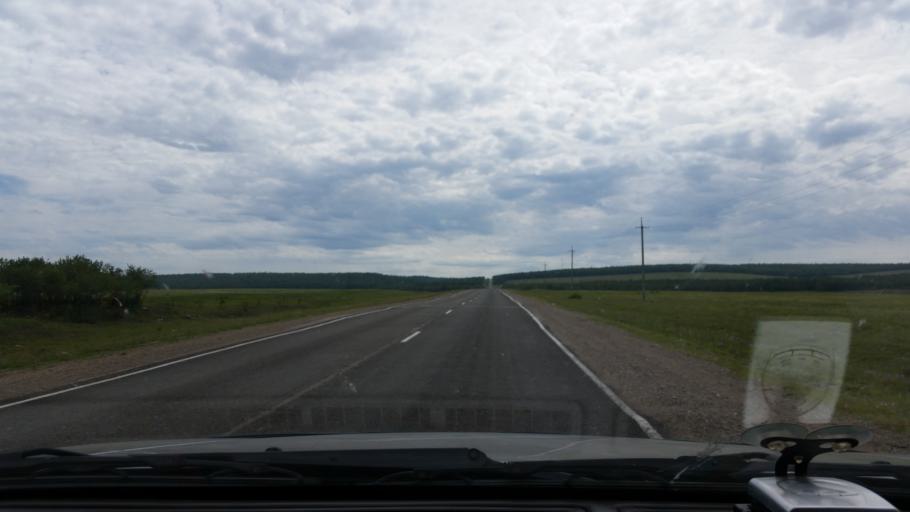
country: RU
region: Irkutsk
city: Bayanday
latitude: 53.0494
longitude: 105.5368
